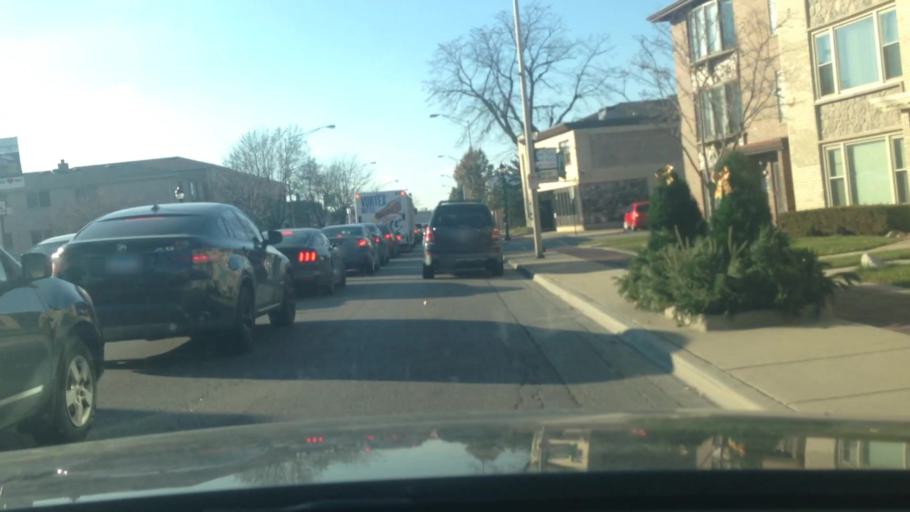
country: US
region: Illinois
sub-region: Cook County
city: River Grove
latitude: 41.9280
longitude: -87.8315
